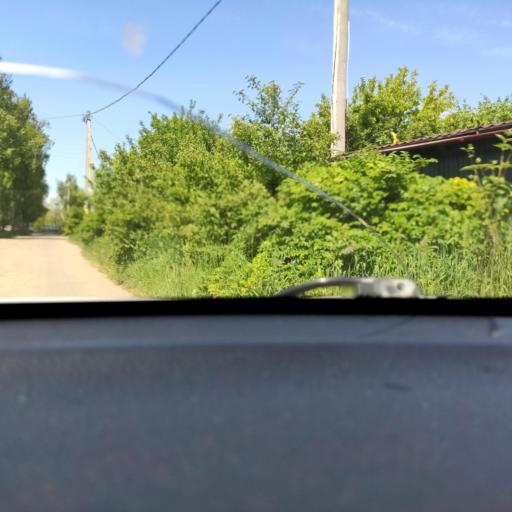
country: RU
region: Tatarstan
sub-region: Gorod Kazan'
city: Kazan
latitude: 55.8600
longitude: 49.1981
